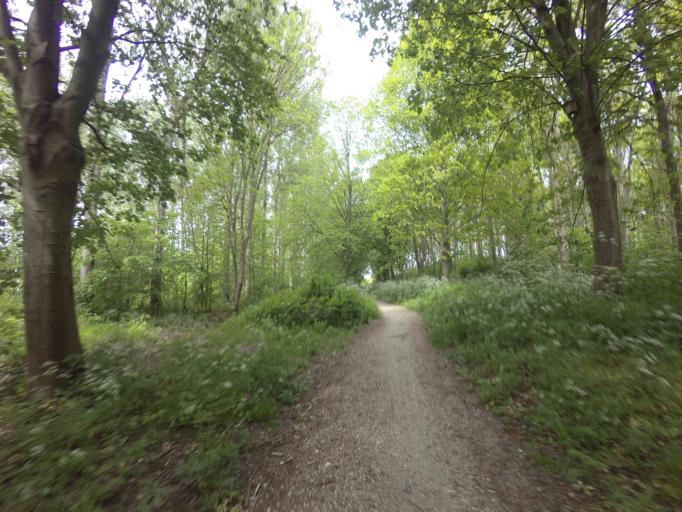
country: NL
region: Friesland
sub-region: Sudwest Fryslan
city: Bolsward
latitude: 53.0960
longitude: 5.4741
